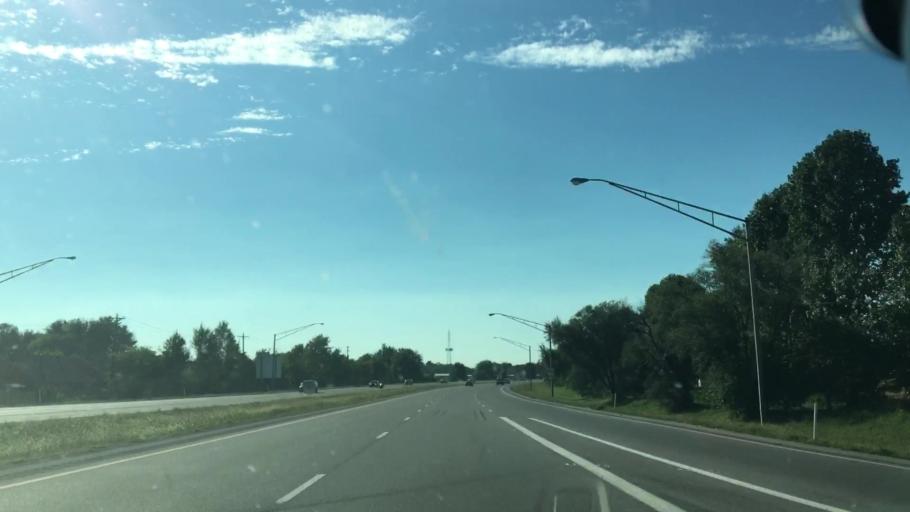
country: US
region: Kentucky
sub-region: Daviess County
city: Owensboro
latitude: 37.7298
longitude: -87.1263
